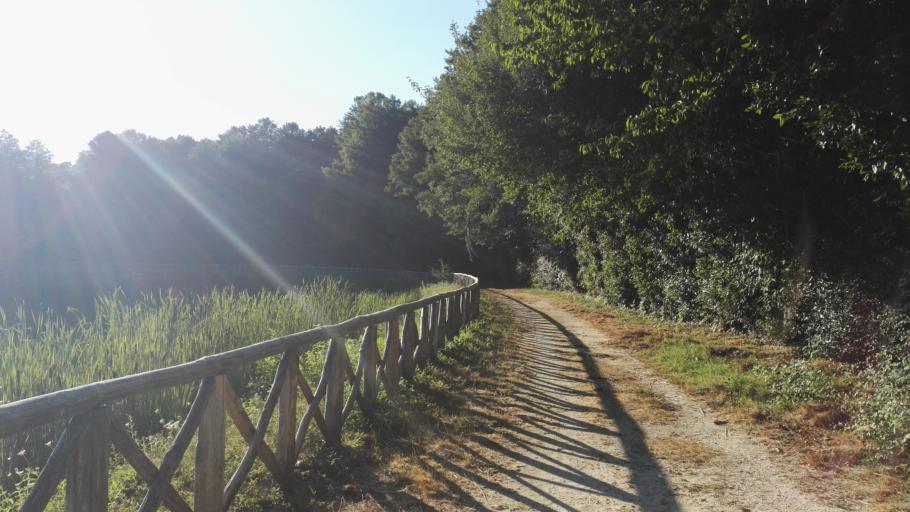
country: IT
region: Calabria
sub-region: Provincia di Vibo-Valentia
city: Mongiana
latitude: 38.5214
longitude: 16.3057
